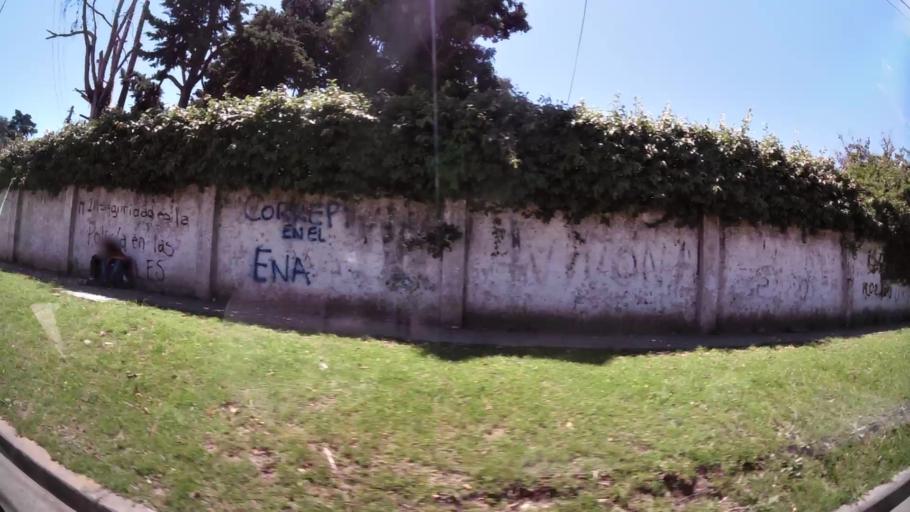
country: AR
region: Buenos Aires
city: Hurlingham
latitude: -34.5158
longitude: -58.7054
